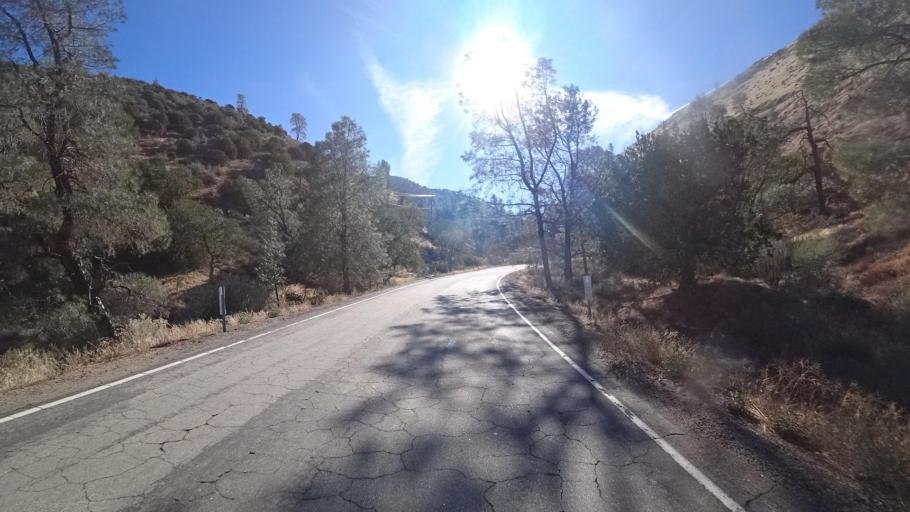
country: US
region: California
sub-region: Kern County
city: Bodfish
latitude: 35.5765
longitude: -118.5036
